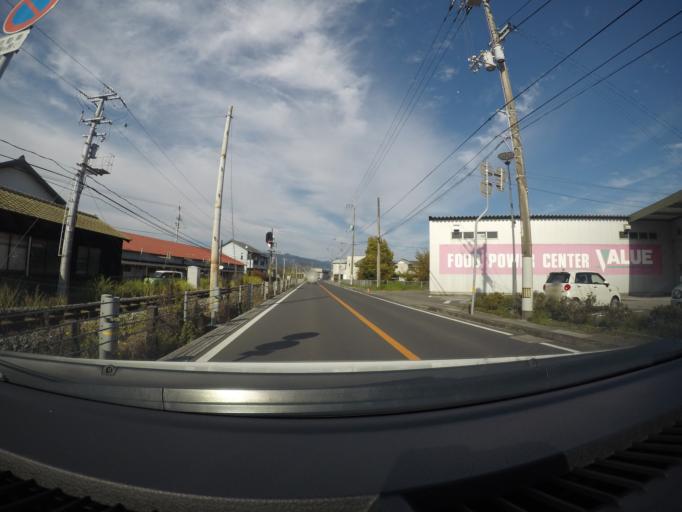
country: JP
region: Kochi
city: Kochi-shi
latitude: 33.6005
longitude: 133.6726
